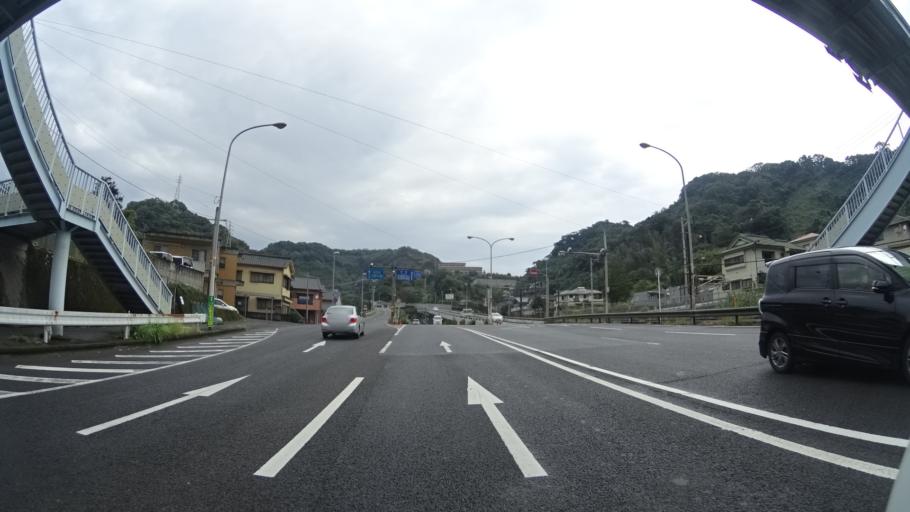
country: JP
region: Kagoshima
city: Kagoshima-shi
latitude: 31.6105
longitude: 130.5700
